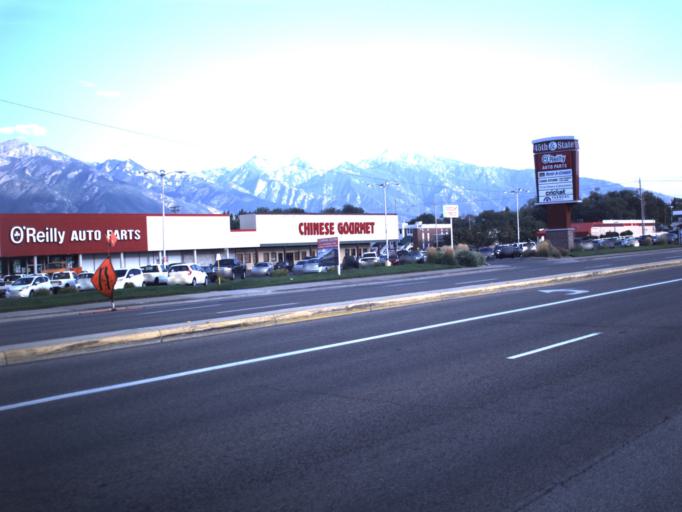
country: US
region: Utah
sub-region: Salt Lake County
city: Murray
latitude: 40.6758
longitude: -111.8884
